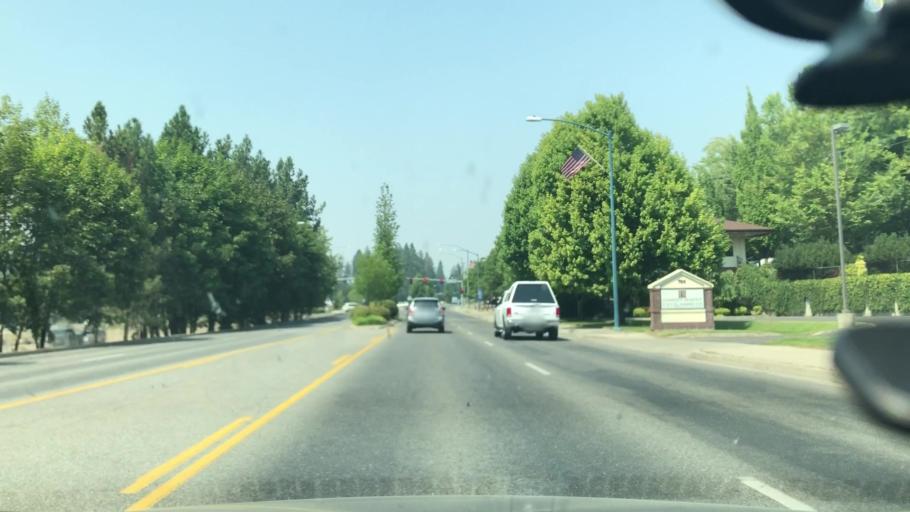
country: US
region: Idaho
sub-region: Kootenai County
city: Coeur d'Alene
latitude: 47.6786
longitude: -116.7902
